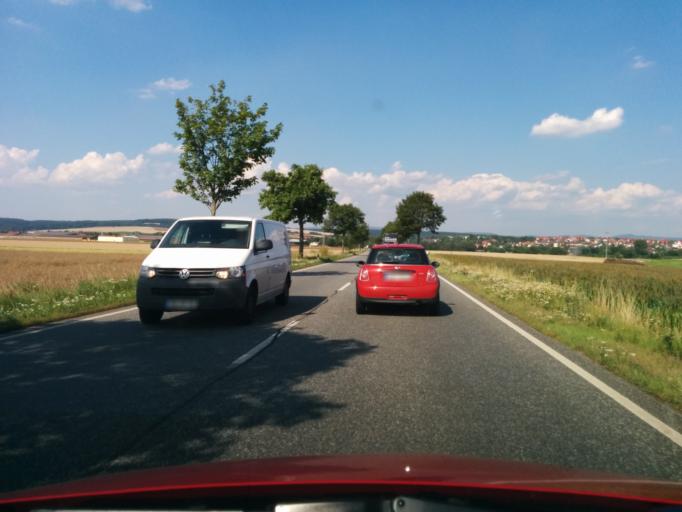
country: DE
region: Lower Saxony
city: Gieboldehausen
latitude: 51.5960
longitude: 10.1985
